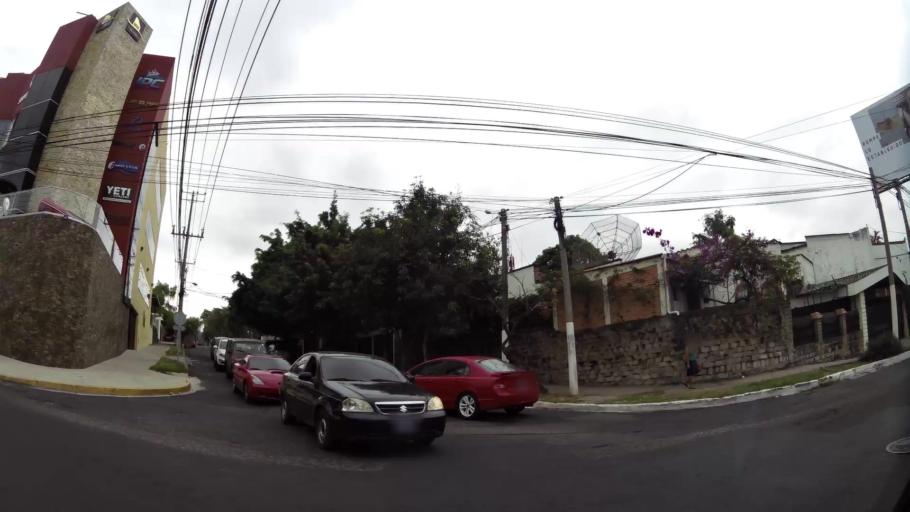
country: SV
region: San Salvador
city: Mejicanos
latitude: 13.7094
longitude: -89.2439
